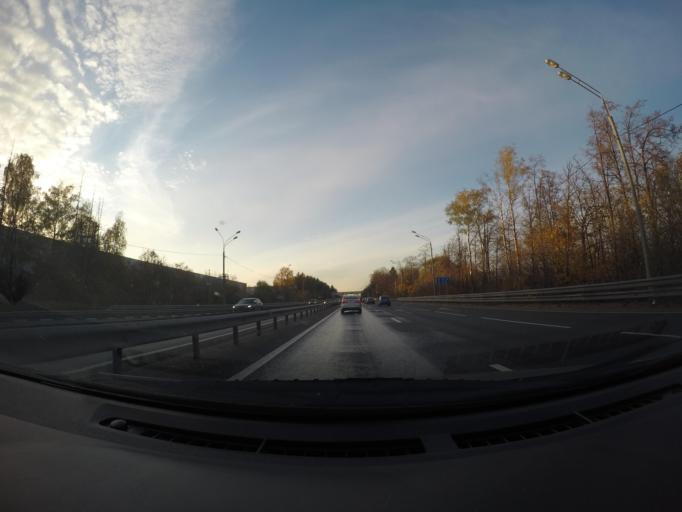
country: RU
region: Moskovskaya
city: Skhodnya
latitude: 55.9812
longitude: 37.2922
